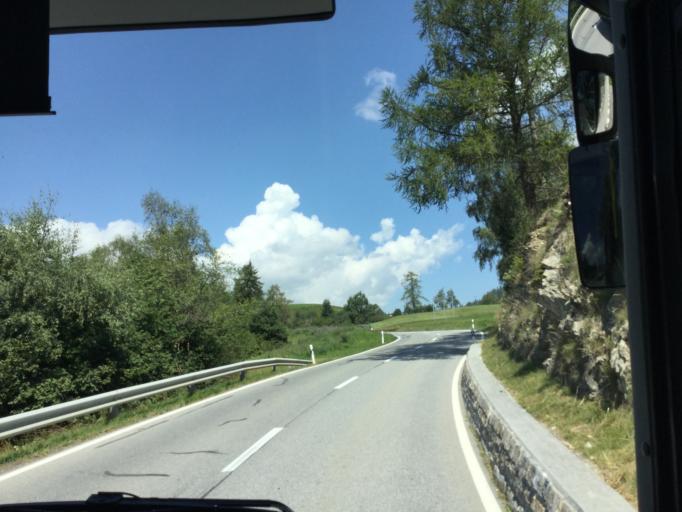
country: CH
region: Grisons
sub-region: Albula District
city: Tiefencastel
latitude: 46.6767
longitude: 9.5674
